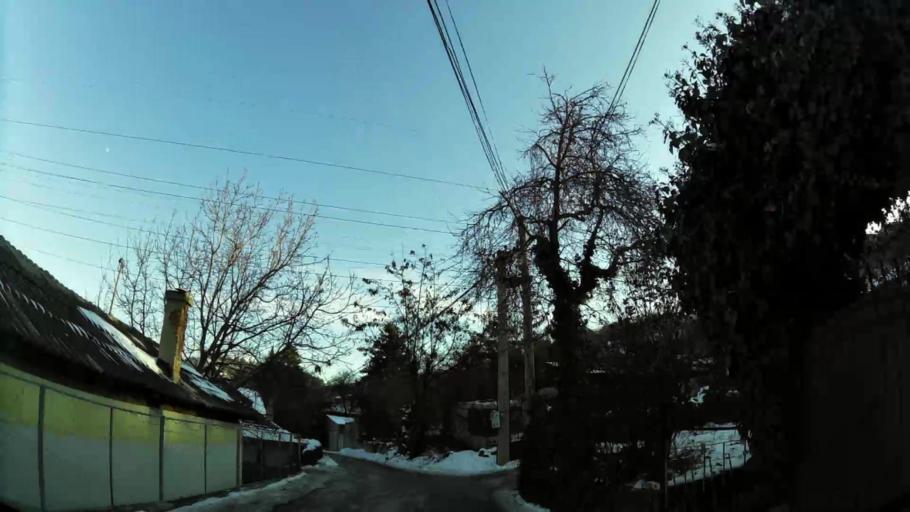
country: MK
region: Karpos
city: Skopje
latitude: 41.9904
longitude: 21.4023
